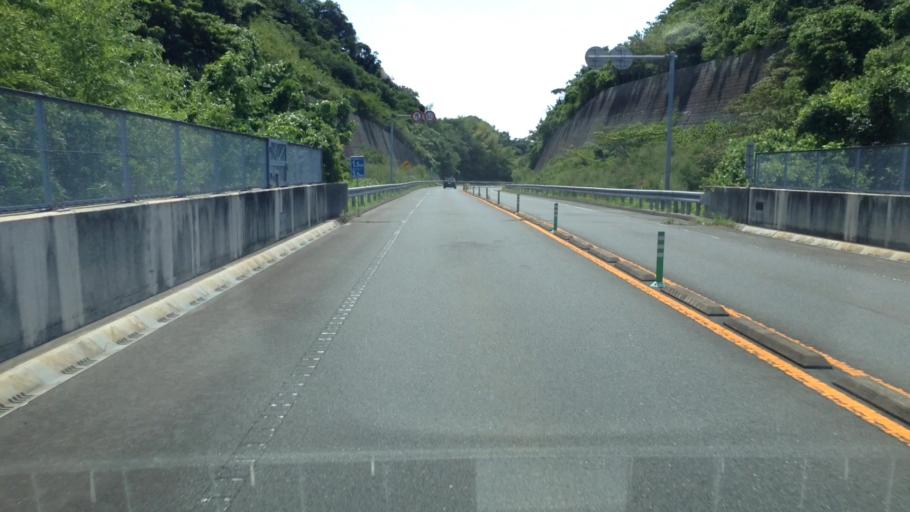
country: JP
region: Kanagawa
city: Yokosuka
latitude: 35.2350
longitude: 139.6507
